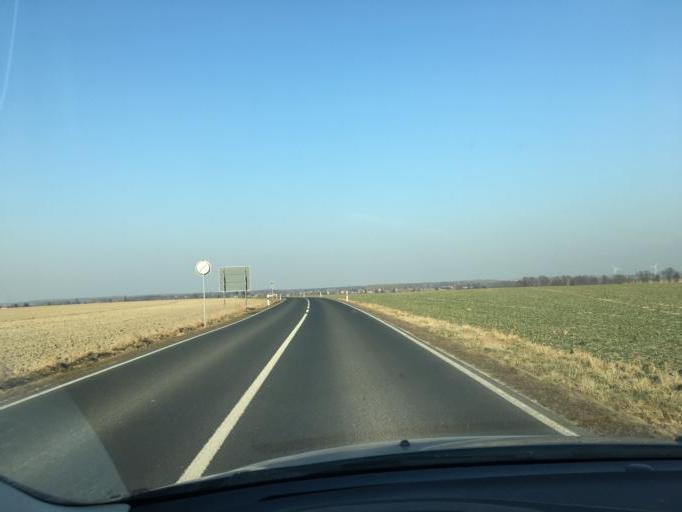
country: DE
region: Saxony
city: Frohburg
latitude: 51.1112
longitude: 12.5810
